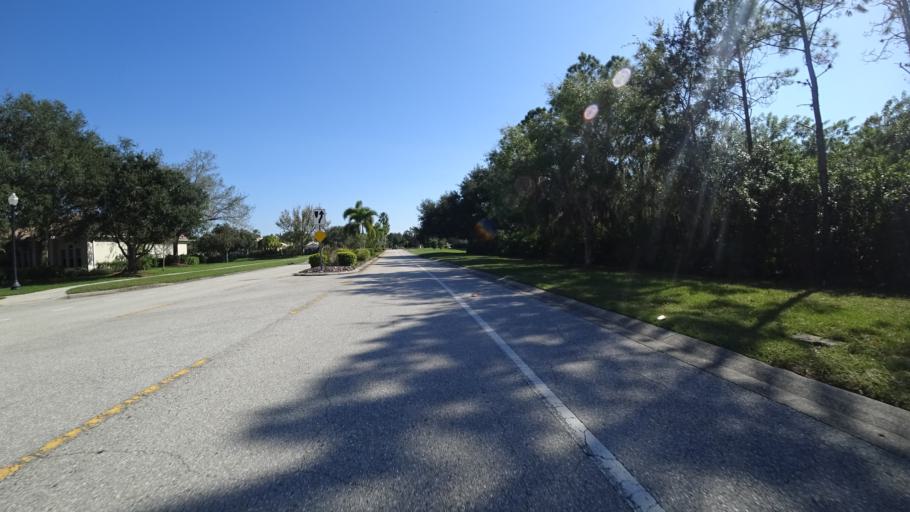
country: US
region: Florida
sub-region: Sarasota County
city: The Meadows
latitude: 27.4094
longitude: -82.4392
